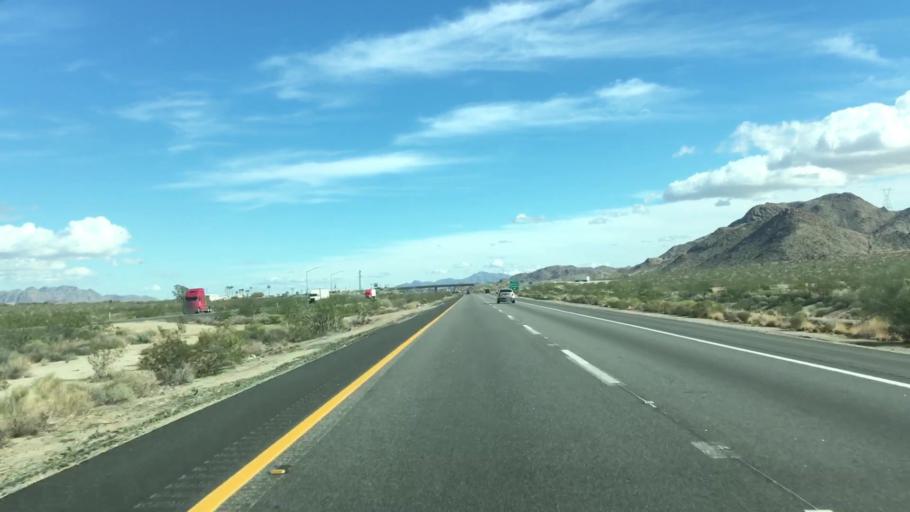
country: US
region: California
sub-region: Riverside County
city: Mecca
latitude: 33.6599
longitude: -115.7315
